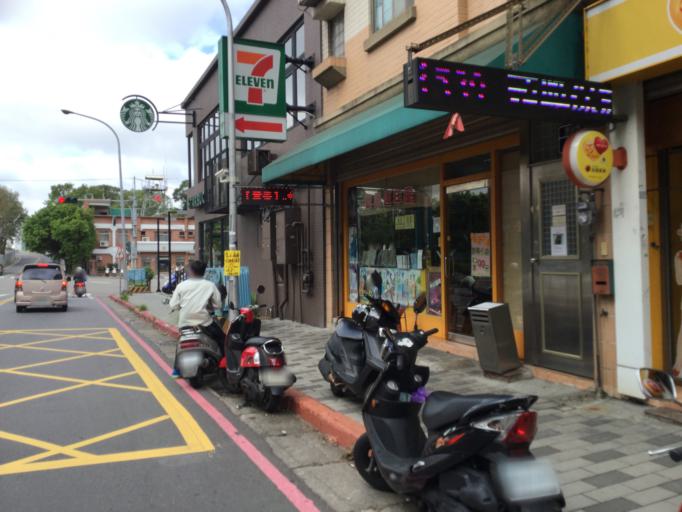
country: TW
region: Taiwan
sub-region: Hsinchu
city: Hsinchu
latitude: 24.7783
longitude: 121.0198
